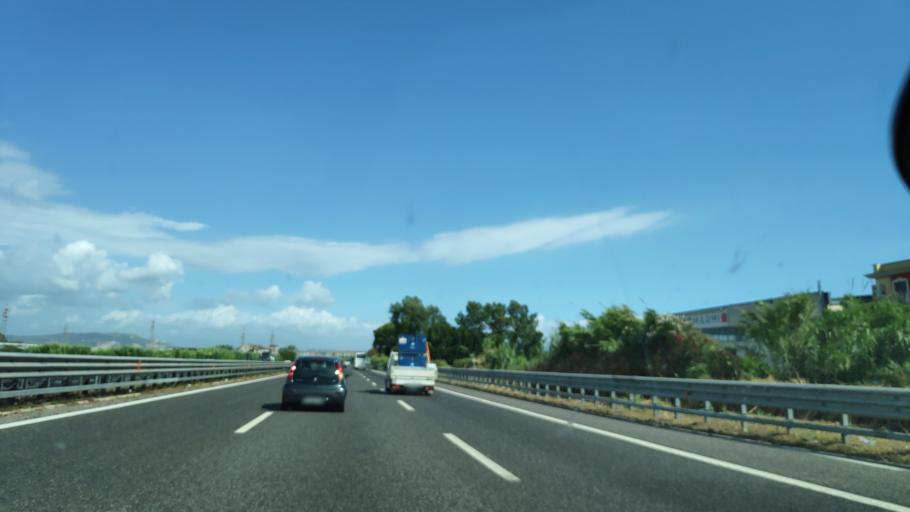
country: IT
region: Campania
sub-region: Provincia di Salerno
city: Sant'Antonio
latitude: 40.6414
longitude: 14.8982
